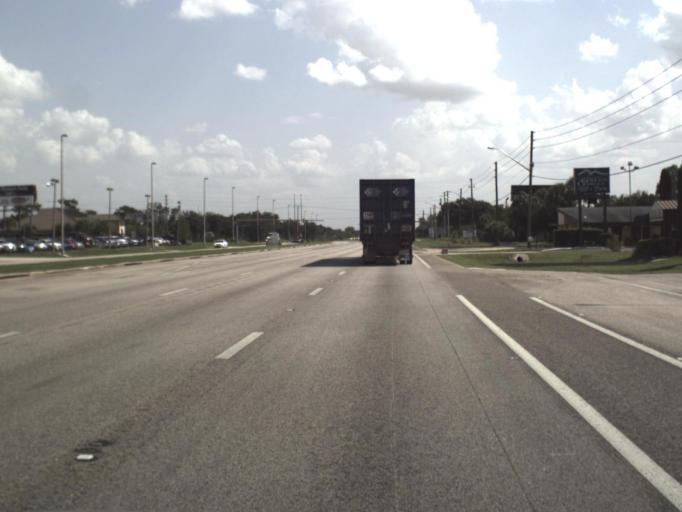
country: US
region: Florida
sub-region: Polk County
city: Lake Wales
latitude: 27.9269
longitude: -81.6073
